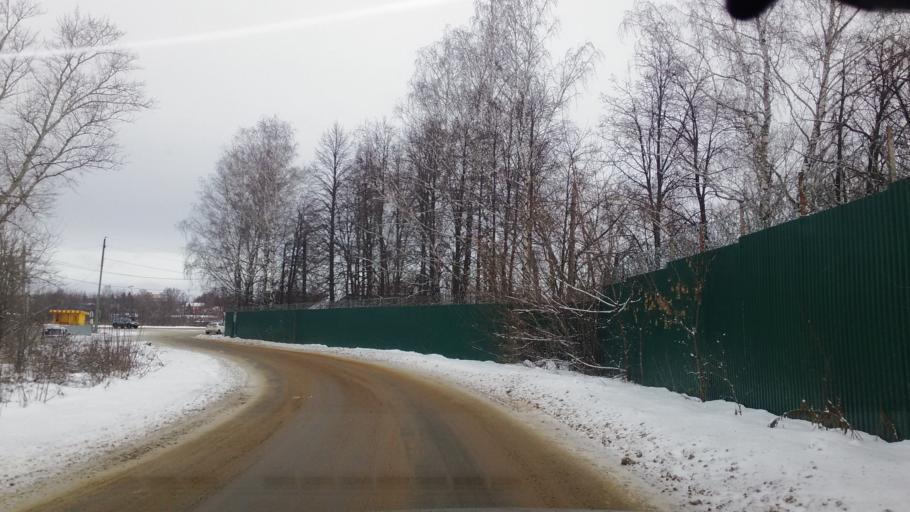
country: RU
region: Tula
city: Bogoroditsk
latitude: 53.7624
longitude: 38.1058
